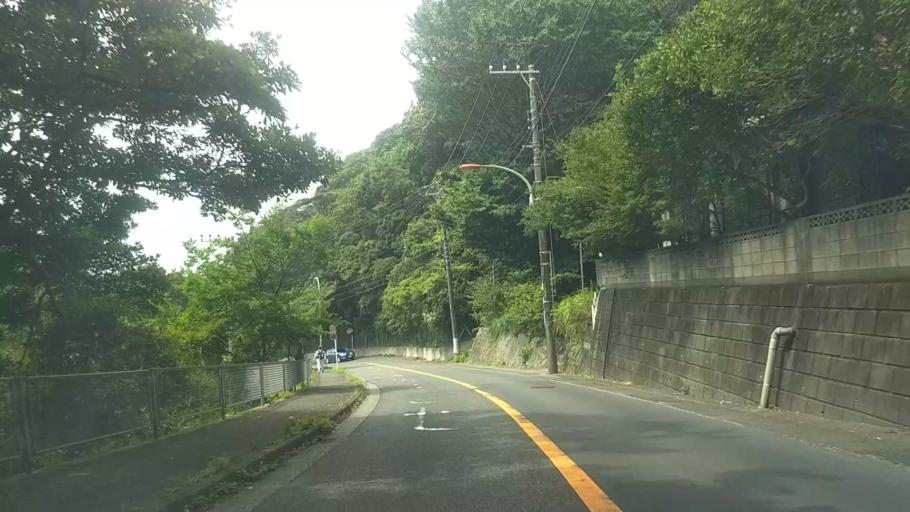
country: JP
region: Kanagawa
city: Yokosuka
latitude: 35.2597
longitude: 139.7171
